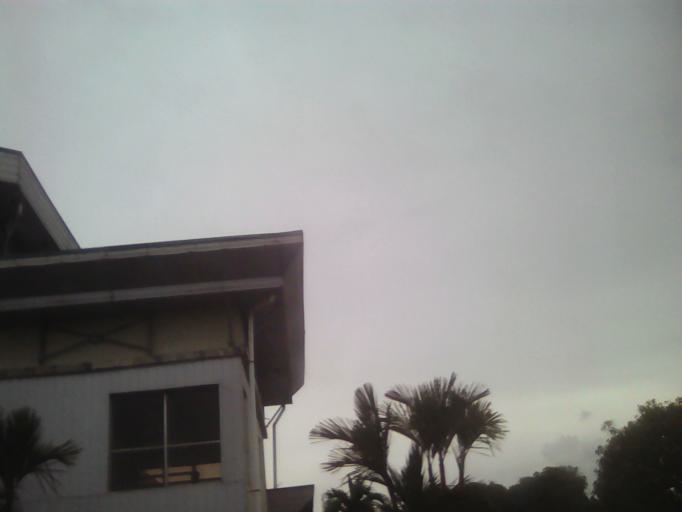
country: MY
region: Penang
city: Perai
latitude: 5.3987
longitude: 100.4248
